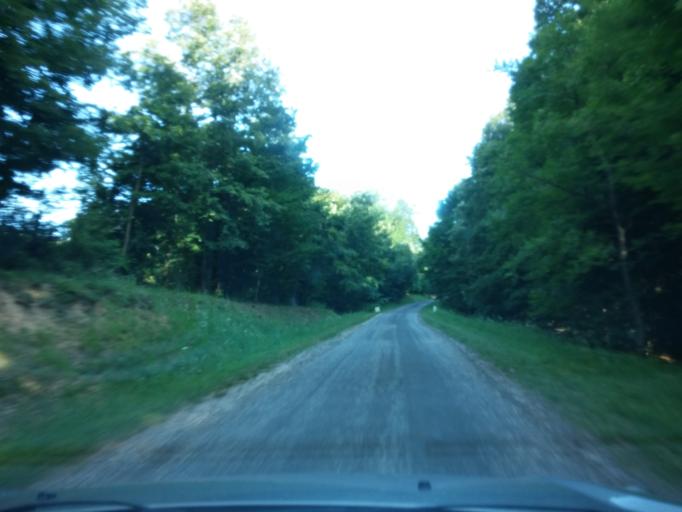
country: HU
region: Somogy
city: Kaposmero
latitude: 46.2542
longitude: 17.7523
